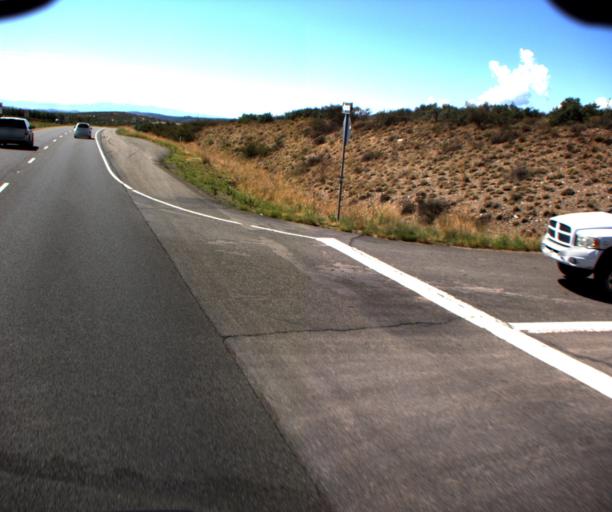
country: US
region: Arizona
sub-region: Yavapai County
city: Mayer
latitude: 34.4509
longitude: -112.2698
